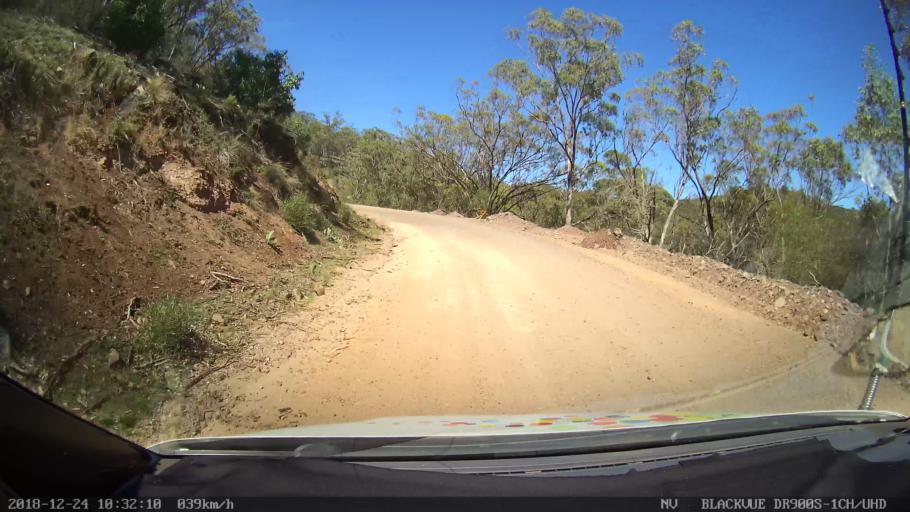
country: AU
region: New South Wales
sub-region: Upper Hunter Shire
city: Merriwa
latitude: -31.8405
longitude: 150.5174
